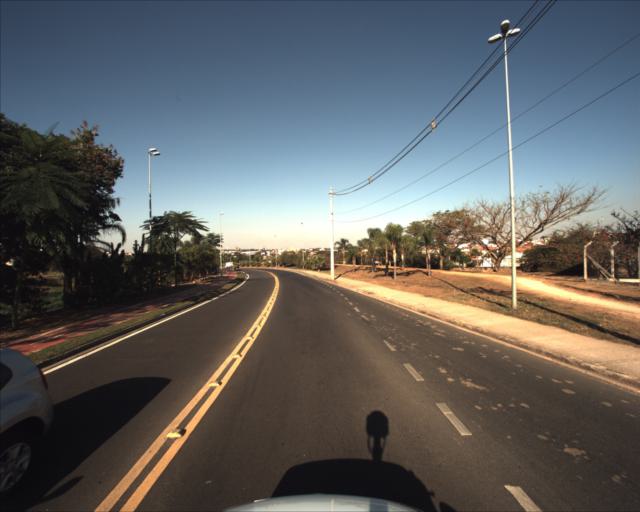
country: BR
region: Sao Paulo
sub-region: Sorocaba
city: Sorocaba
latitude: -23.4700
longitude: -47.4519
